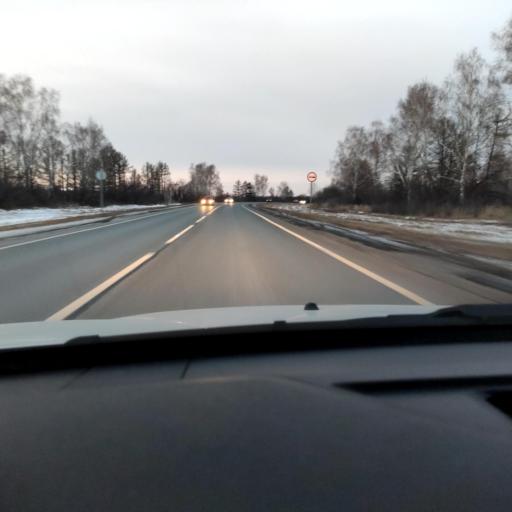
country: RU
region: Samara
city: Volzhskiy
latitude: 53.4753
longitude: 50.1183
